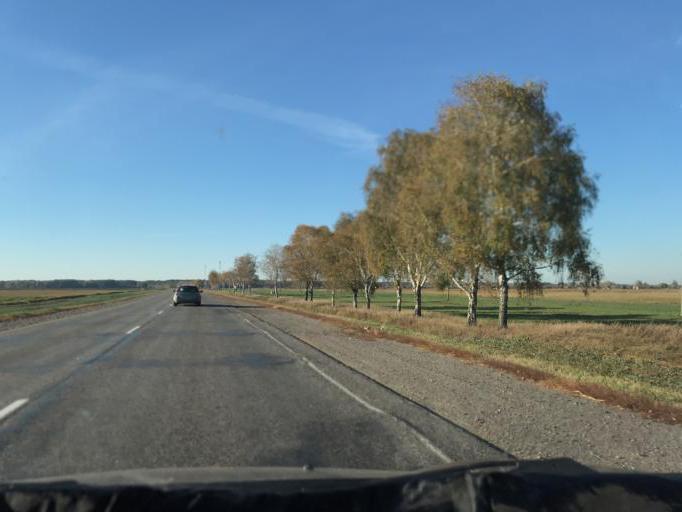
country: BY
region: Gomel
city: Kalinkavichy
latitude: 52.1583
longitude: 29.2367
